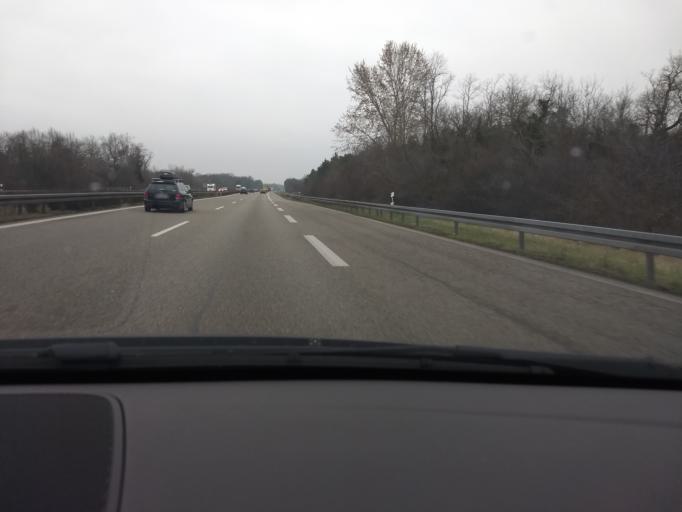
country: FR
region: Alsace
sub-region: Departement du Haut-Rhin
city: Chalampe
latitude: 47.7920
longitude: 7.5394
